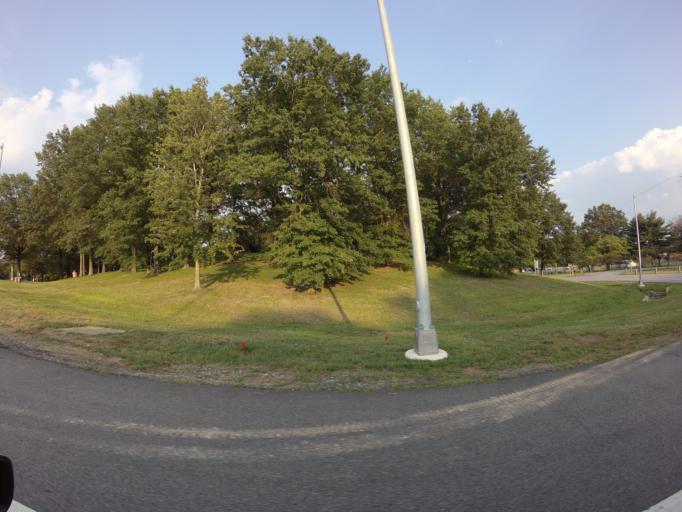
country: US
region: Maryland
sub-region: Howard County
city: Savage
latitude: 39.1447
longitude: -76.8464
